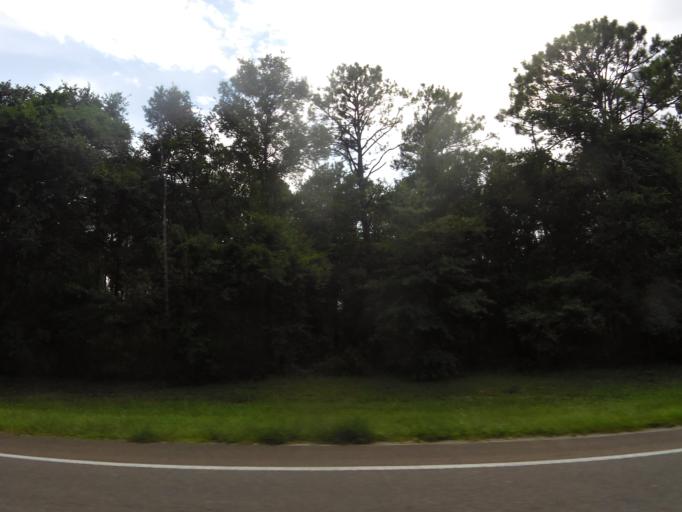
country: US
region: Florida
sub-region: Nassau County
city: Fernandina Beach
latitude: 30.6203
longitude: -81.4615
